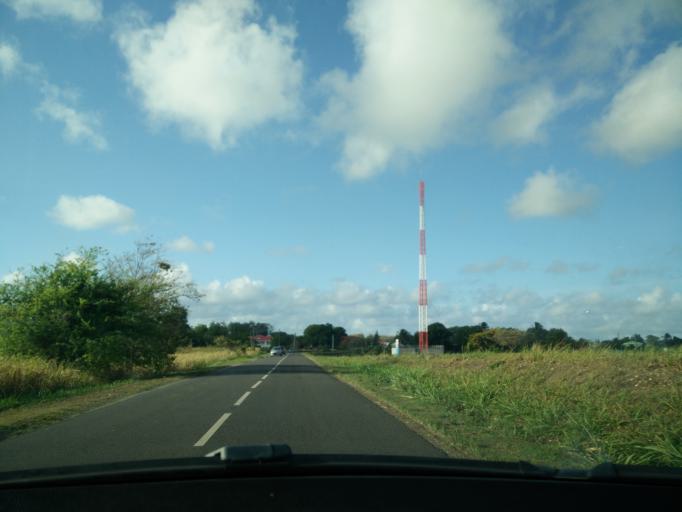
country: GP
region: Guadeloupe
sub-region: Guadeloupe
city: Le Moule
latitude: 16.3041
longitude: -61.3669
